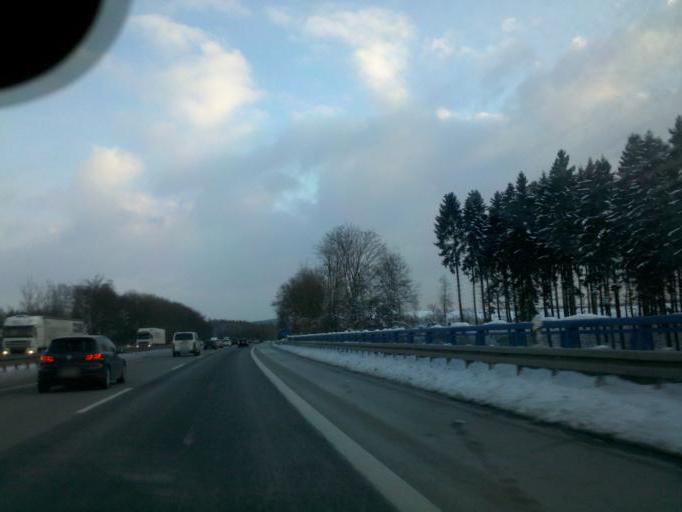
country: DE
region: North Rhine-Westphalia
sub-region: Regierungsbezirk Arnsberg
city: Wenden
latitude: 50.9598
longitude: 7.8469
